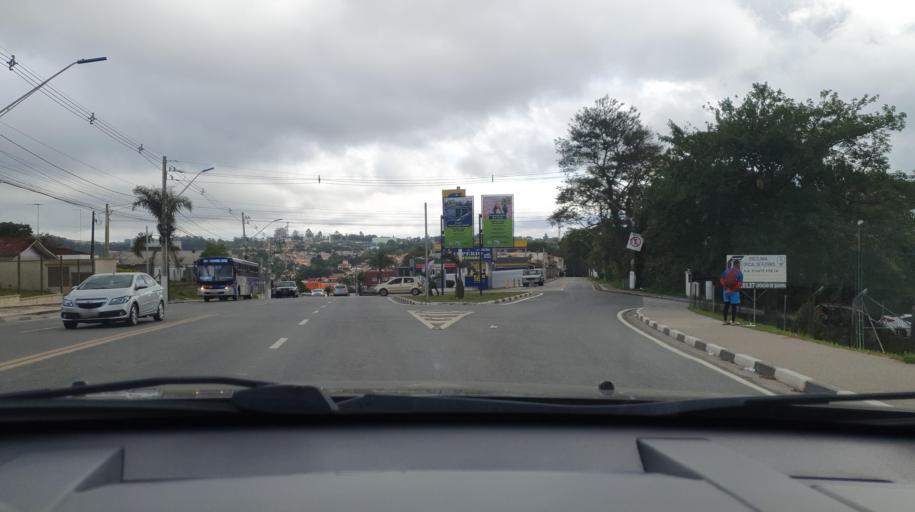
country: BR
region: Sao Paulo
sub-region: Vargem Grande Paulista
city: Vargem Grande Paulista
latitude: -23.6812
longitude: -47.0177
